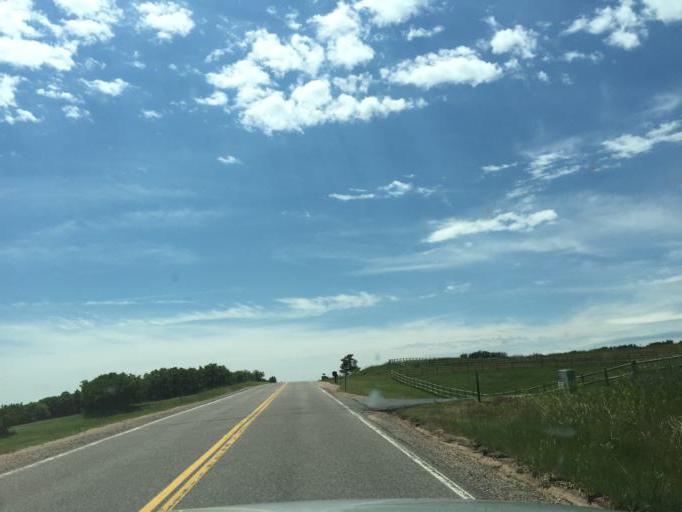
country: US
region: Colorado
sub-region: Douglas County
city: Perry Park
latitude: 39.3021
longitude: -104.9160
